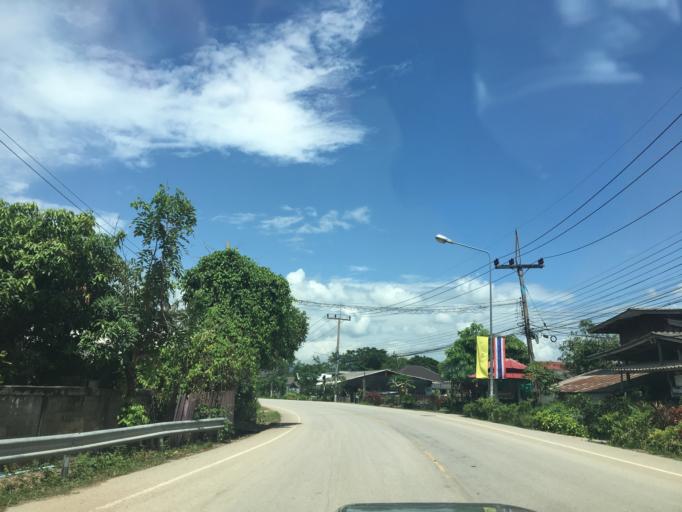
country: TH
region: Chiang Rai
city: Pa Daet
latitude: 19.4955
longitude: 99.9592
